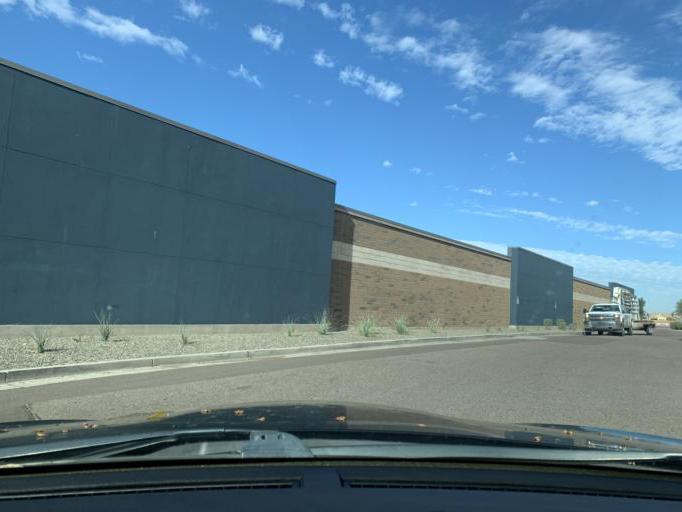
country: US
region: Arizona
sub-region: Maricopa County
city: Gilbert
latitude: 33.3341
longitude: -111.7224
